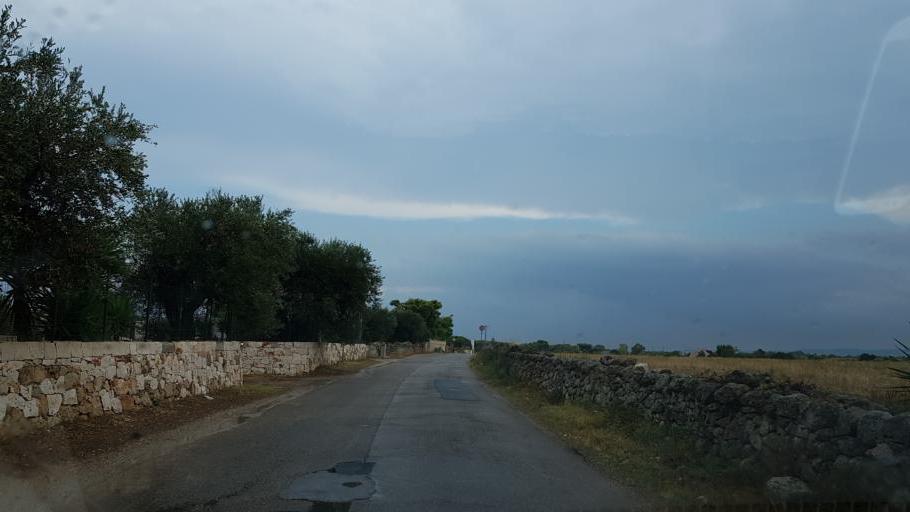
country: IT
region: Apulia
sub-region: Provincia di Bari
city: Monopoli
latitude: 40.9311
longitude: 17.3251
